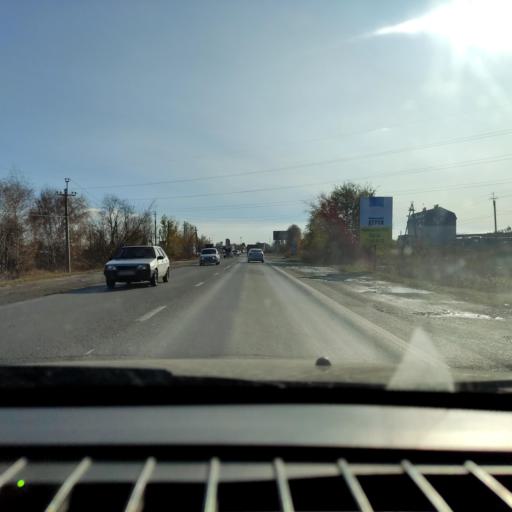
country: RU
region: Samara
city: Tol'yatti
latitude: 53.5663
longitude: 49.3497
